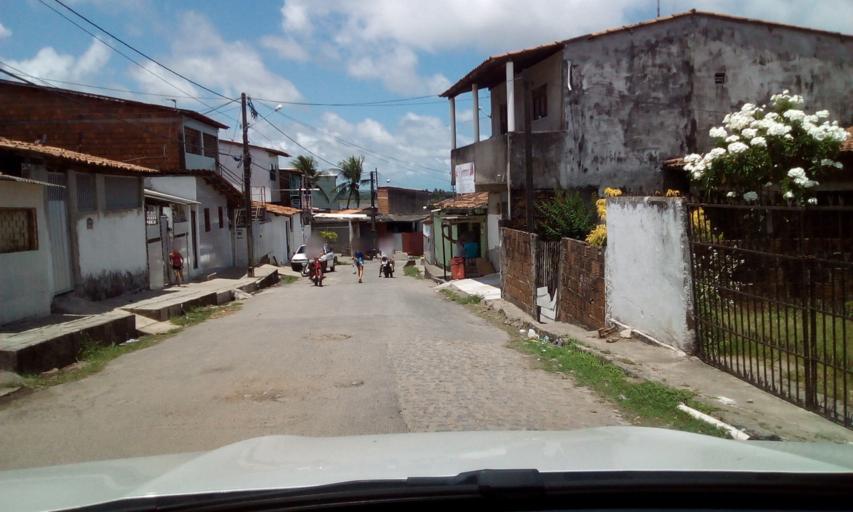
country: BR
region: Paraiba
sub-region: Joao Pessoa
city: Joao Pessoa
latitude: -7.0956
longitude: -34.8639
